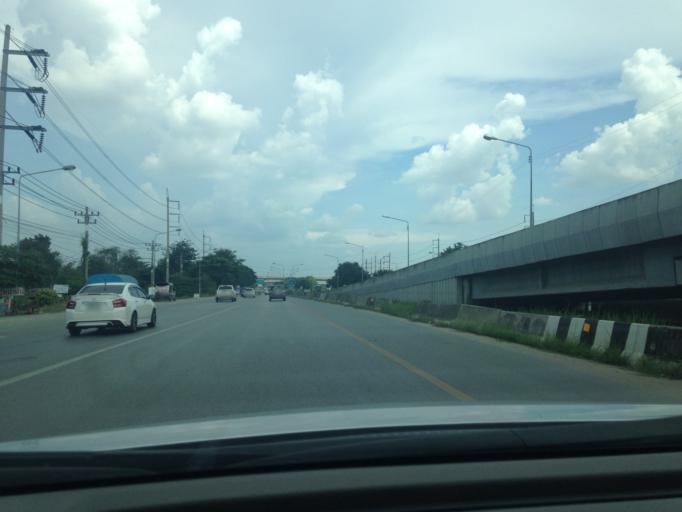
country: TH
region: Pathum Thani
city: Sam Khok
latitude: 14.0663
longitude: 100.5722
